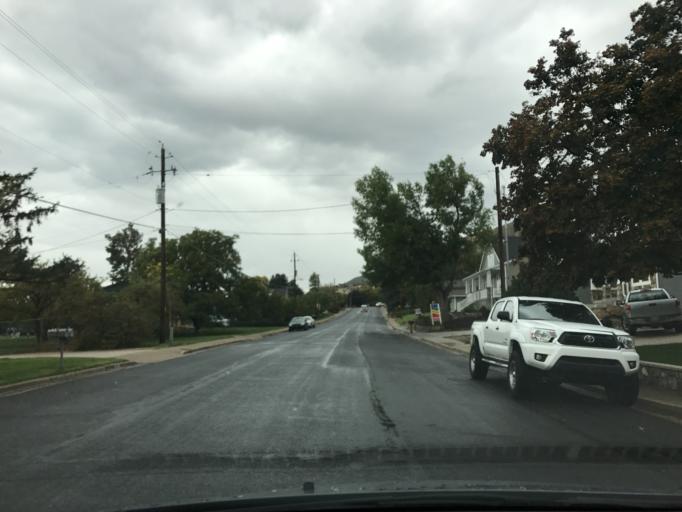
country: US
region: Utah
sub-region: Davis County
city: Farmington
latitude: 40.9960
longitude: -111.8942
